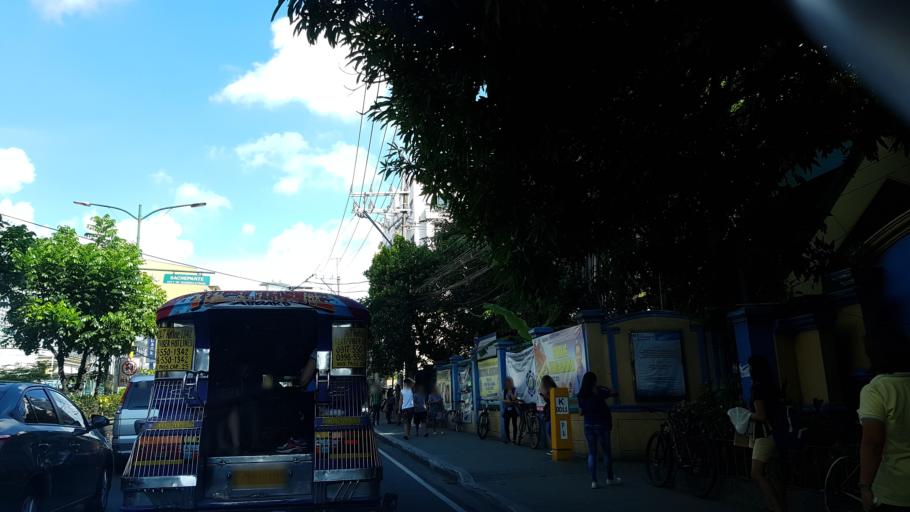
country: PH
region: Metro Manila
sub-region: Mandaluyong
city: Mandaluyong City
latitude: 14.5748
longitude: 121.0425
